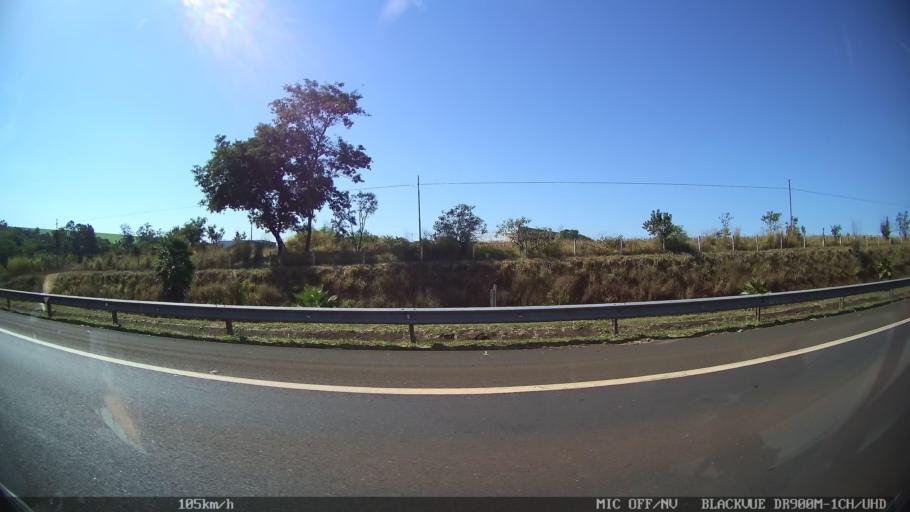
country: BR
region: Sao Paulo
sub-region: Batatais
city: Batatais
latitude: -20.8538
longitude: -47.6008
